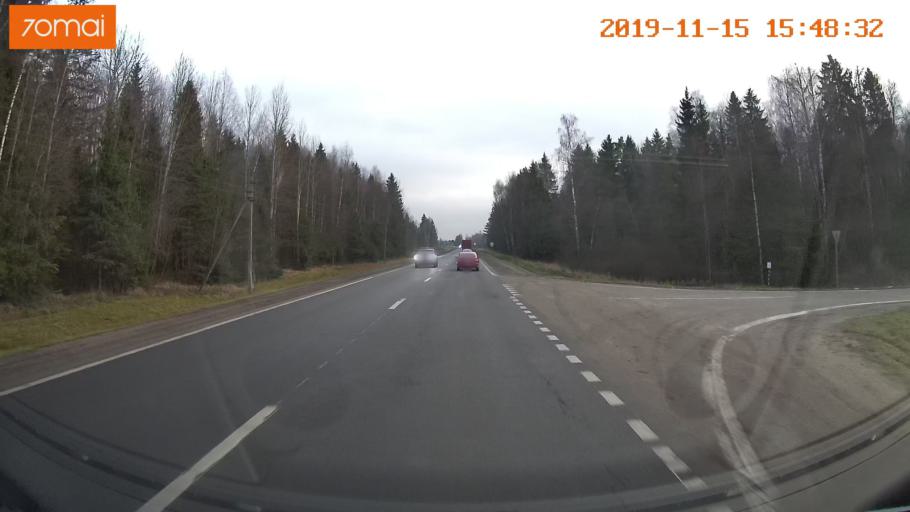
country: RU
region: Jaroslavl
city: Danilov
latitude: 57.9261
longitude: 40.0065
